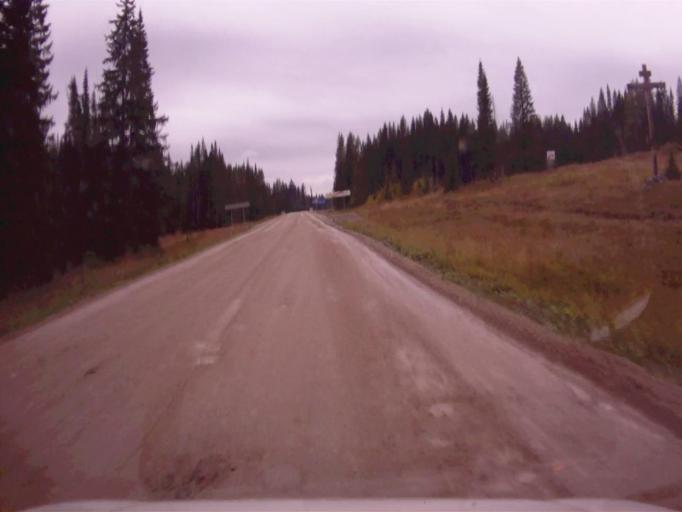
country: RU
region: Chelyabinsk
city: Nyazepetrovsk
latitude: 56.0583
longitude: 59.5575
